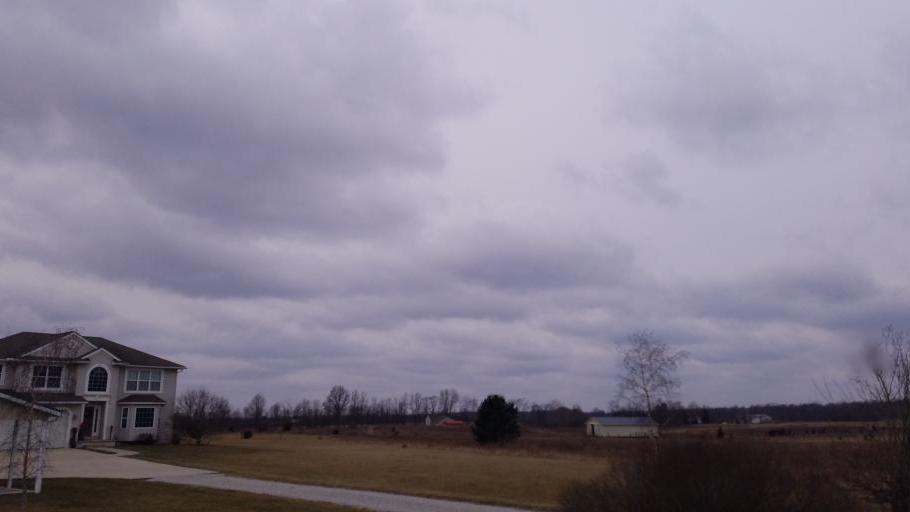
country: US
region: Ohio
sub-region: Crawford County
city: Crestline
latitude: 40.7304
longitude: -82.7031
